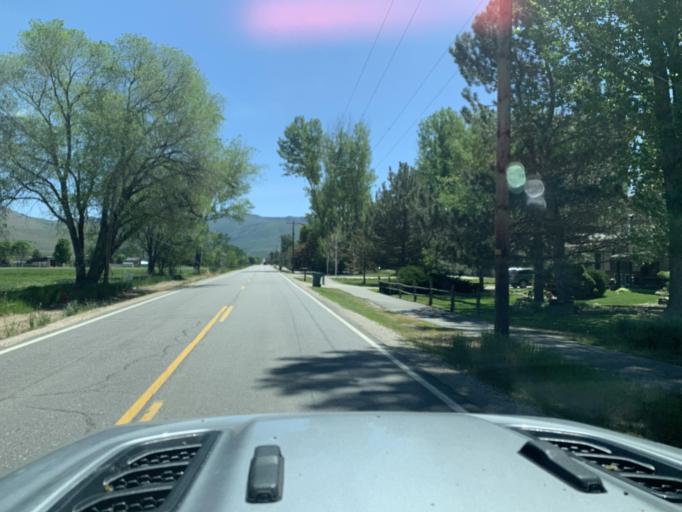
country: US
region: Utah
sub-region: Weber County
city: Wolf Creek
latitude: 41.2933
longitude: -111.8048
